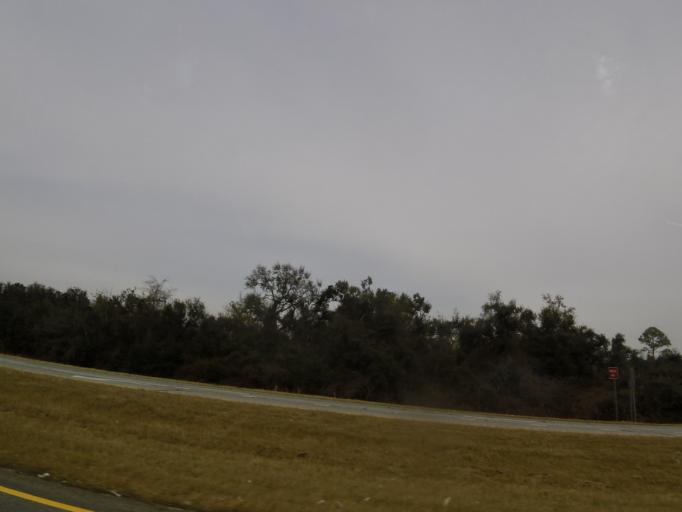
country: US
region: Georgia
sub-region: Seminole County
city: Donalsonville
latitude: 30.9775
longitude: -84.7504
